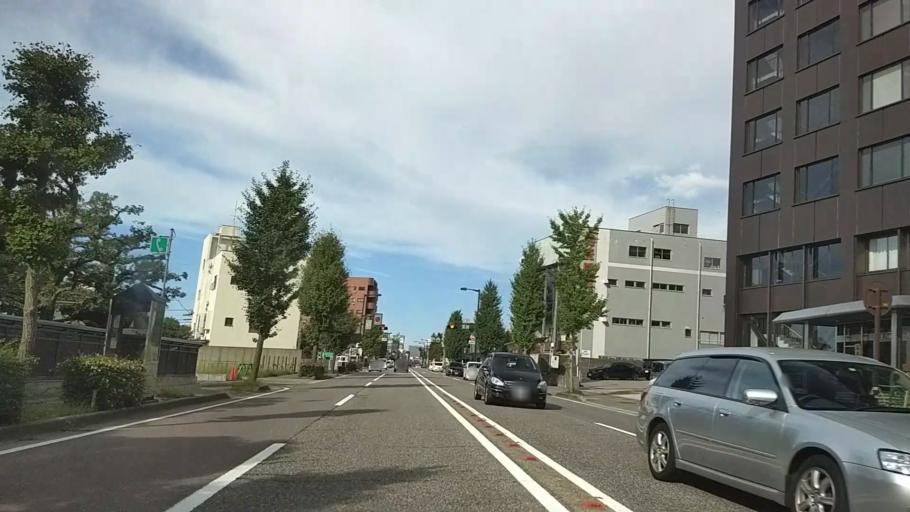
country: JP
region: Ishikawa
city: Nonoichi
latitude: 36.5478
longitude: 136.6431
